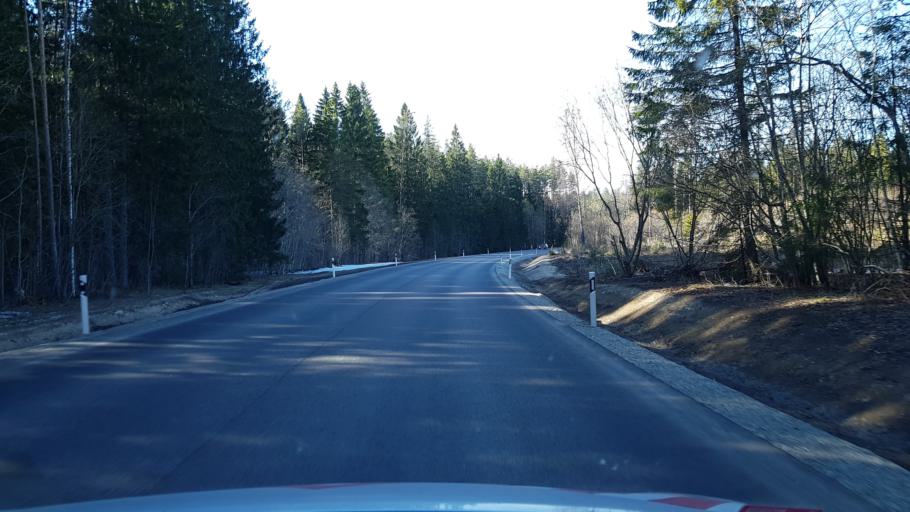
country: EE
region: Laeaene-Virumaa
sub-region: Vinni vald
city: Vinni
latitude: 59.1337
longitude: 26.6009
